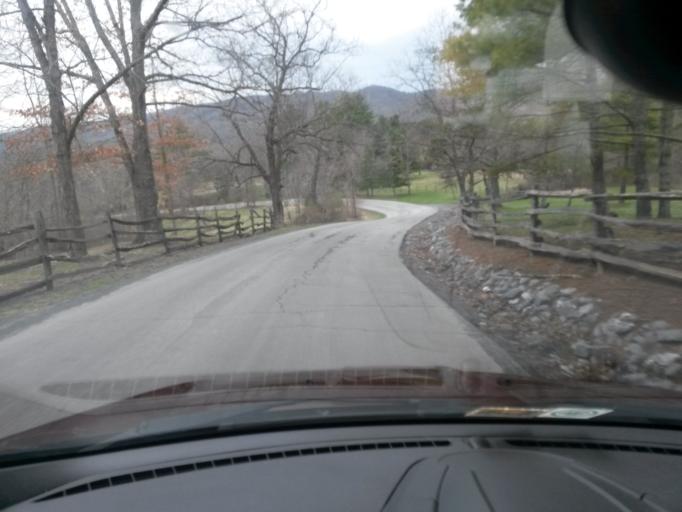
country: US
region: Virginia
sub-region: Bath County
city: Warm Springs
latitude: 38.0541
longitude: -79.8485
